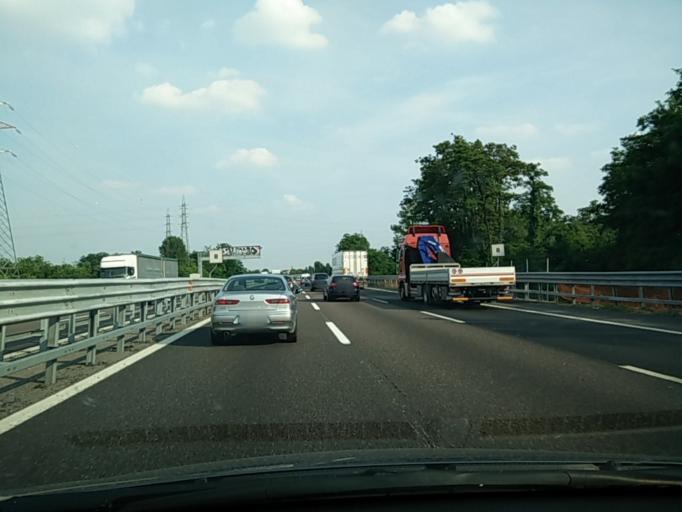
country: IT
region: Lombardy
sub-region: Citta metropolitana di Milano
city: Figino
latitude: 45.4795
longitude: 9.0745
